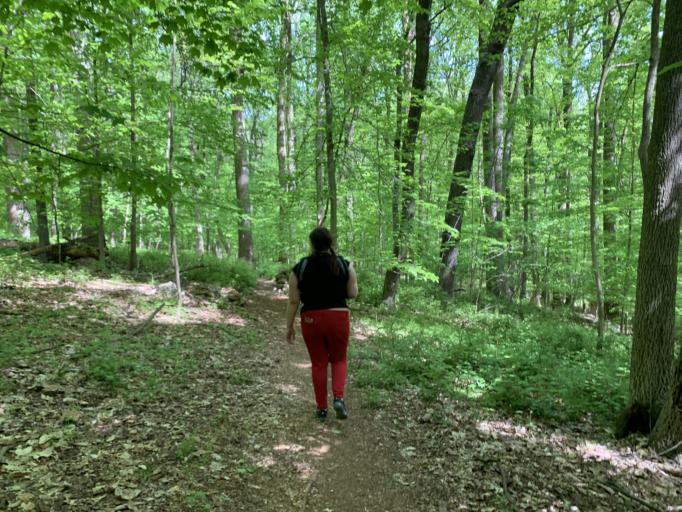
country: US
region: Maryland
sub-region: Harford County
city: South Bel Air
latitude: 39.6190
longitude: -76.2758
